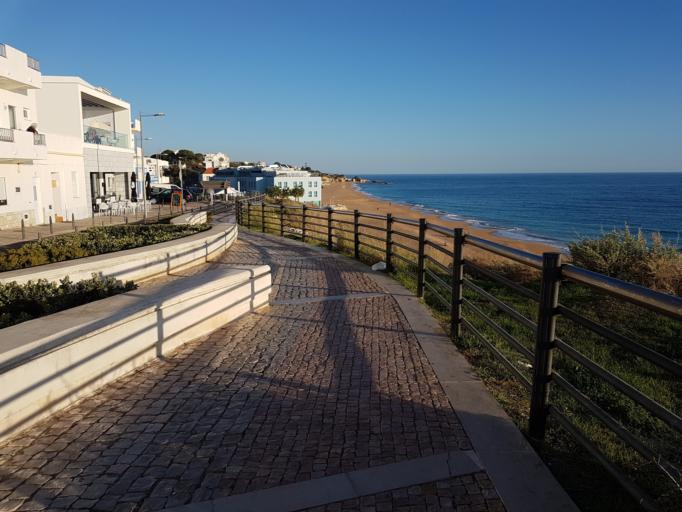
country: PT
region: Faro
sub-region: Albufeira
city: Albufeira
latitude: 37.0864
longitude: -8.2468
